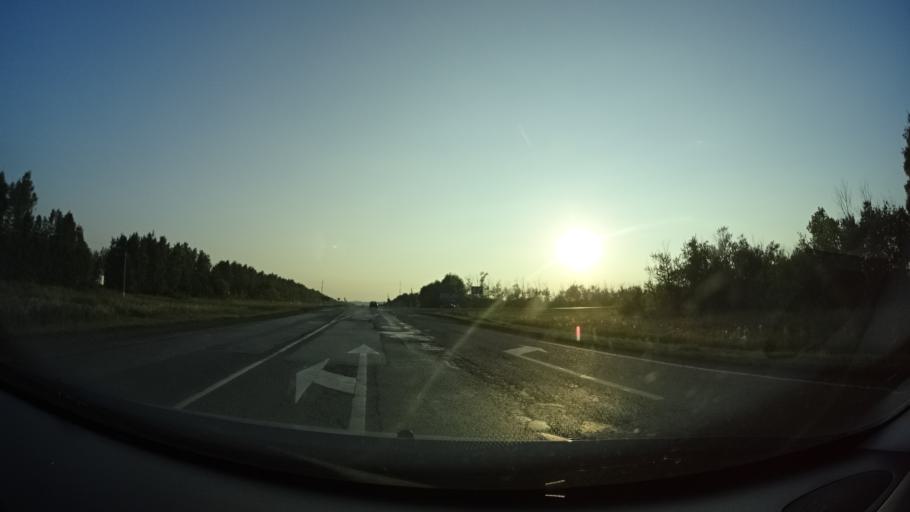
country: RU
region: Samara
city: Isakly
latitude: 54.0063
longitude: 51.6175
